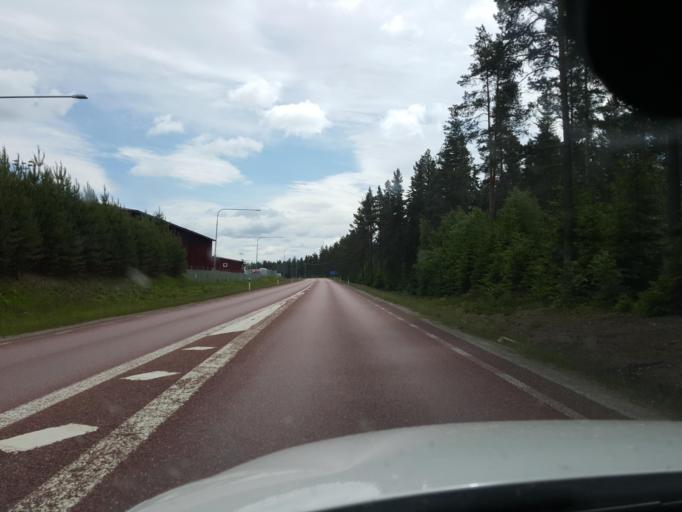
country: SE
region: Gaevleborg
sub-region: Ljusdals Kommun
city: Farila
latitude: 61.8074
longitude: 15.7763
